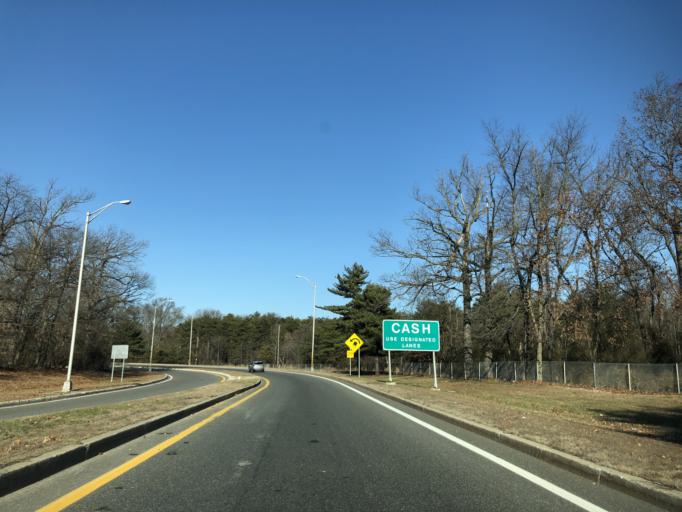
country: US
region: Pennsylvania
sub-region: Delaware County
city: Chester
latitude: 39.8037
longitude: -75.3468
